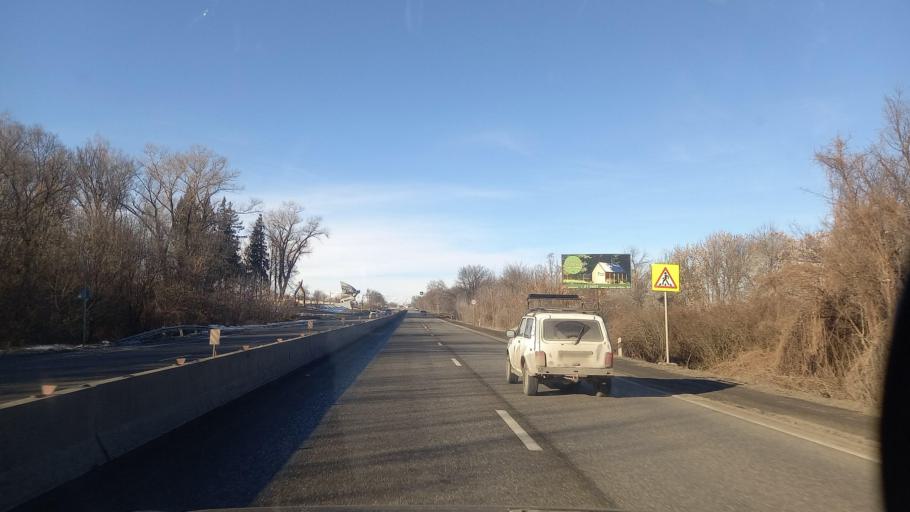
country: RU
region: North Ossetia
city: Gizel'
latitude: 43.0287
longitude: 44.5888
